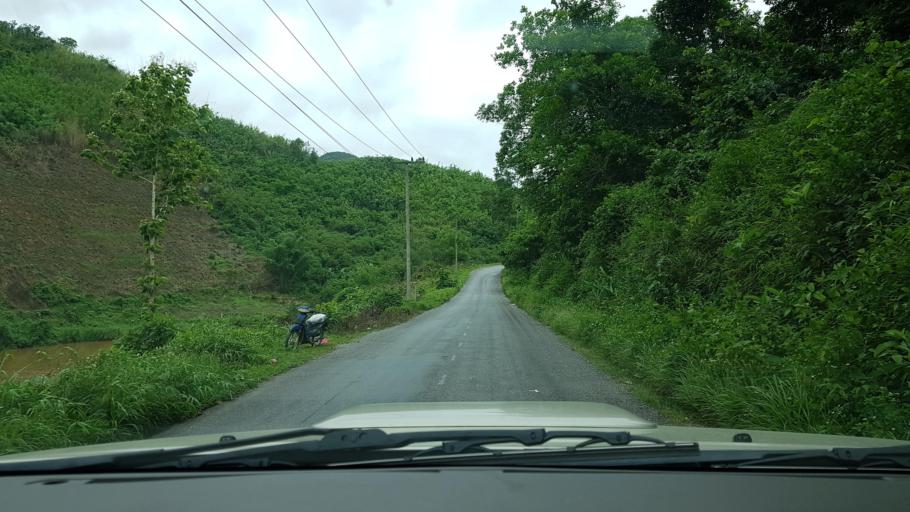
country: LA
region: Oudomxai
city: Muang La
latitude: 21.0370
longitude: 102.2397
